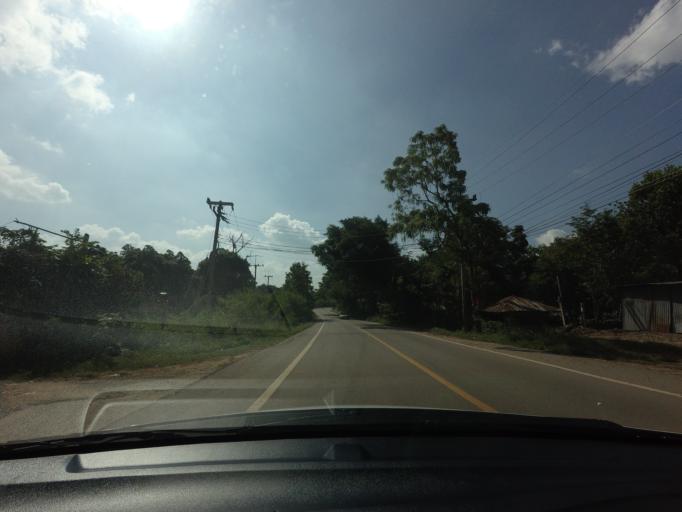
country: TH
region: Nakhon Ratchasima
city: Wang Nam Khiao
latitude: 14.4593
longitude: 101.6606
